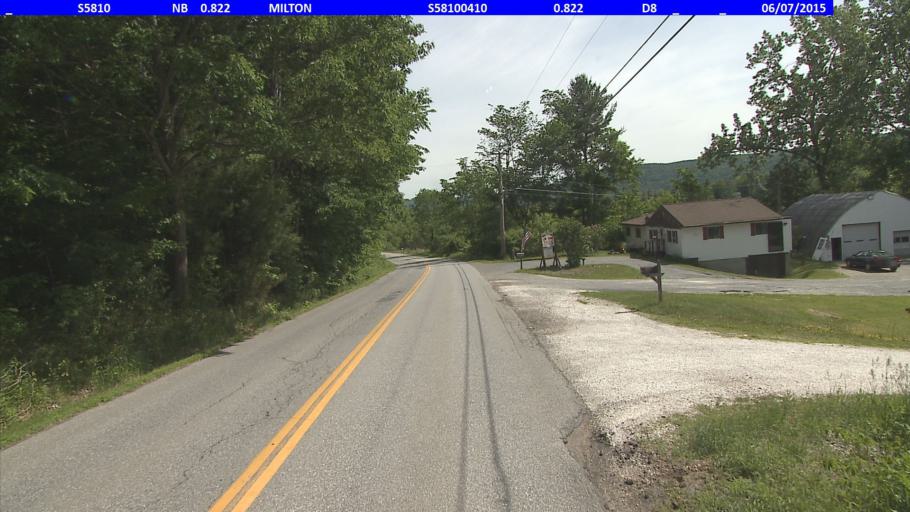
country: US
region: Vermont
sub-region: Chittenden County
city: Milton
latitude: 44.5935
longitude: -73.1302
